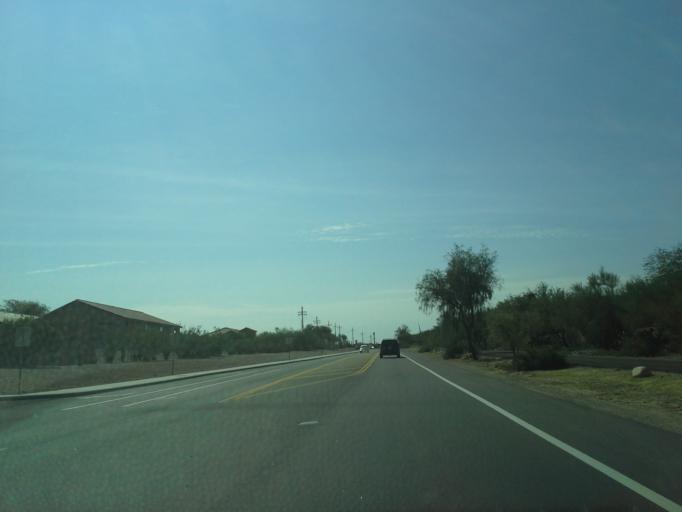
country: US
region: Arizona
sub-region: Pima County
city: Flowing Wells
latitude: 32.2431
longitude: -111.0205
